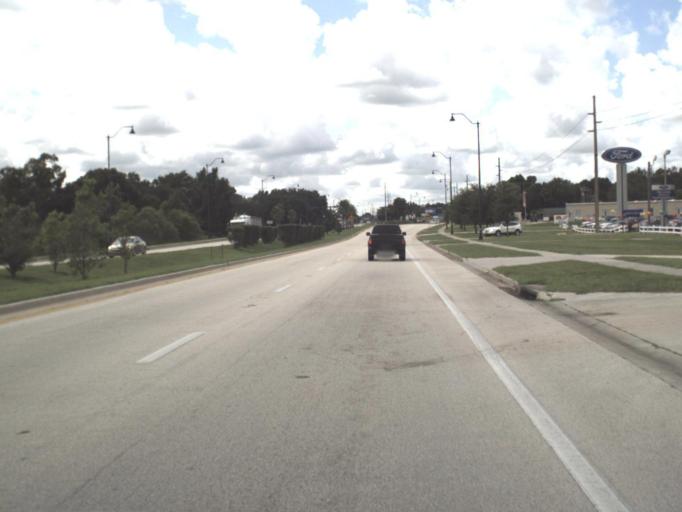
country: US
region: Florida
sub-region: Hardee County
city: Wauchula
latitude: 27.5603
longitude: -81.8138
